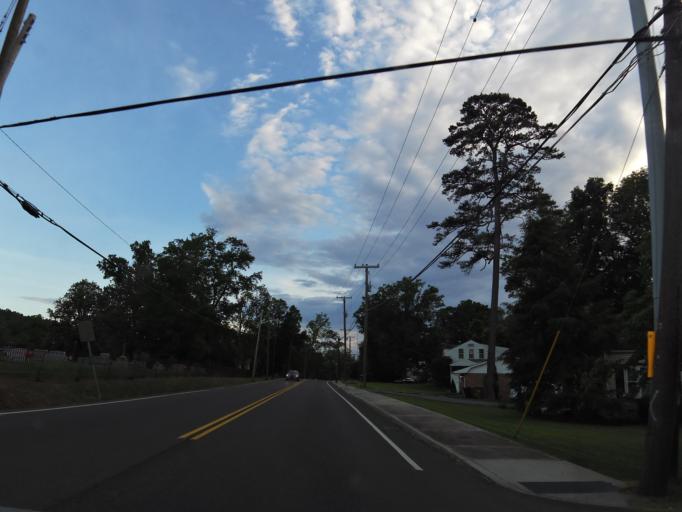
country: US
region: Tennessee
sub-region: Knox County
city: Knoxville
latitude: 36.0341
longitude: -83.9154
